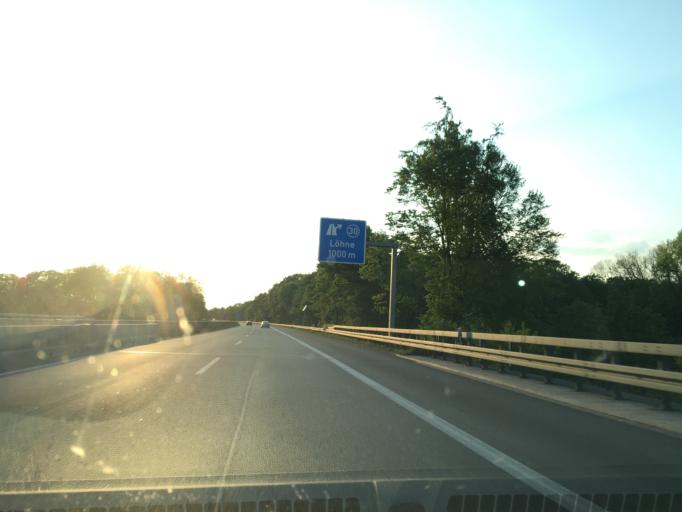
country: DE
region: North Rhine-Westphalia
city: Loehne
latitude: 52.2054
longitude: 8.7307
